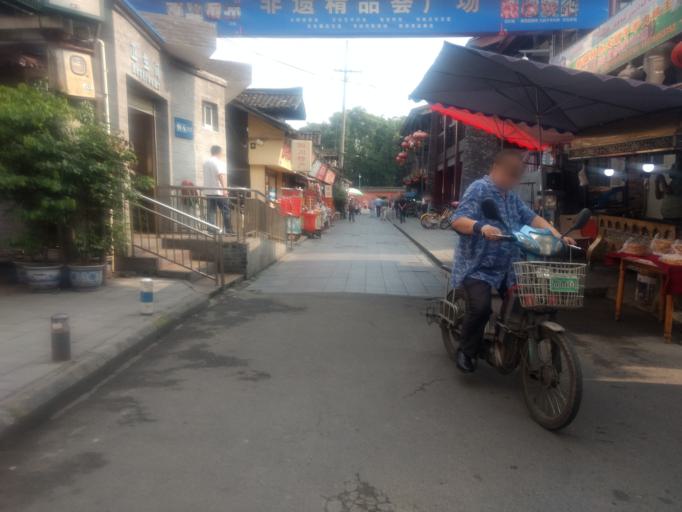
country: CN
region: Sichuan
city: Chengdu
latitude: 30.6760
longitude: 104.0698
